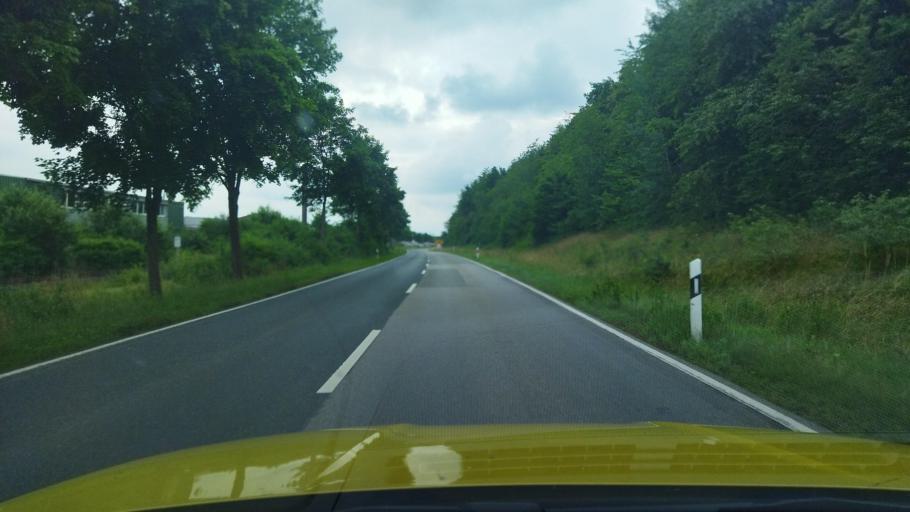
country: DE
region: Bavaria
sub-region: Regierungsbezirk Mittelfranken
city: Gunzenhausen
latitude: 49.1256
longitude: 10.7750
